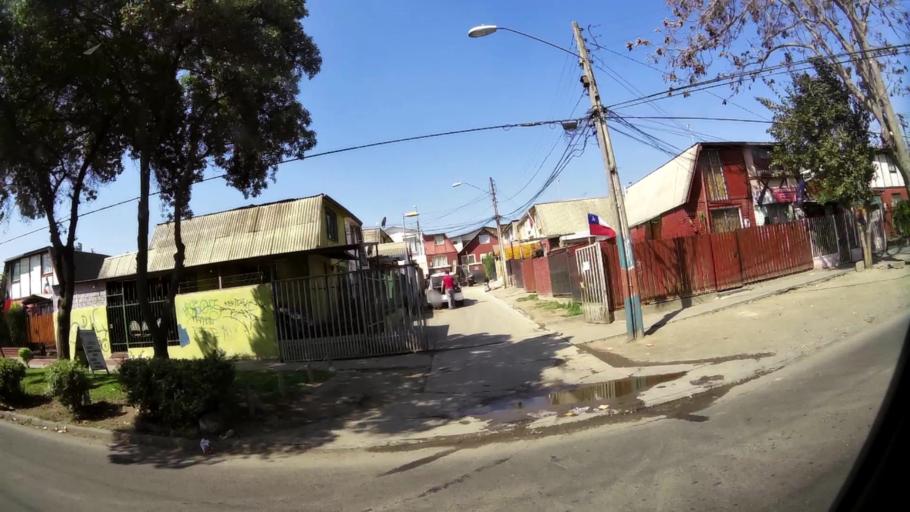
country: CL
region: Santiago Metropolitan
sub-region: Provincia de Santiago
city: Lo Prado
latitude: -33.5023
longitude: -70.7755
